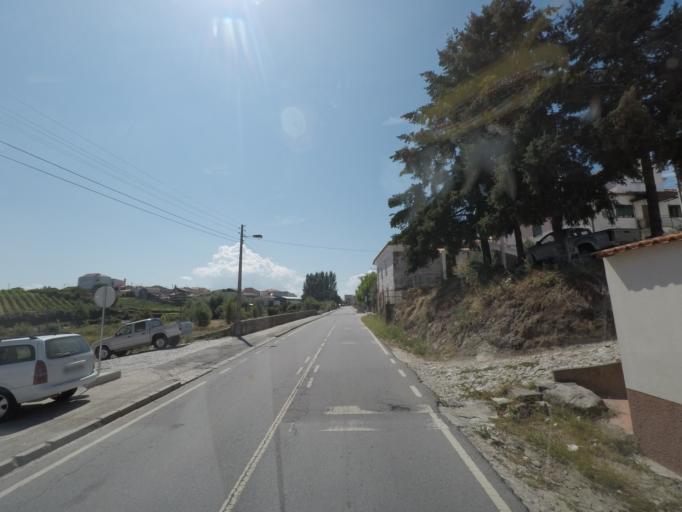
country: PT
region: Vila Real
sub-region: Sabrosa
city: Sabrosa
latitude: 41.2667
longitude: -7.4795
